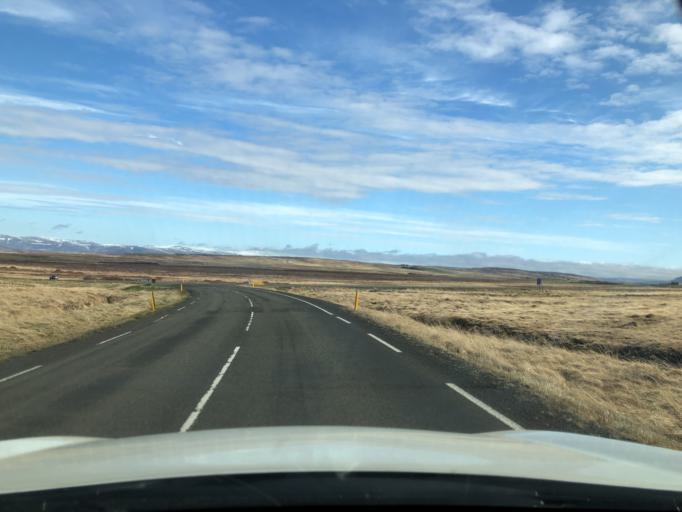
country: IS
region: West
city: Borgarnes
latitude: 65.0889
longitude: -21.7450
